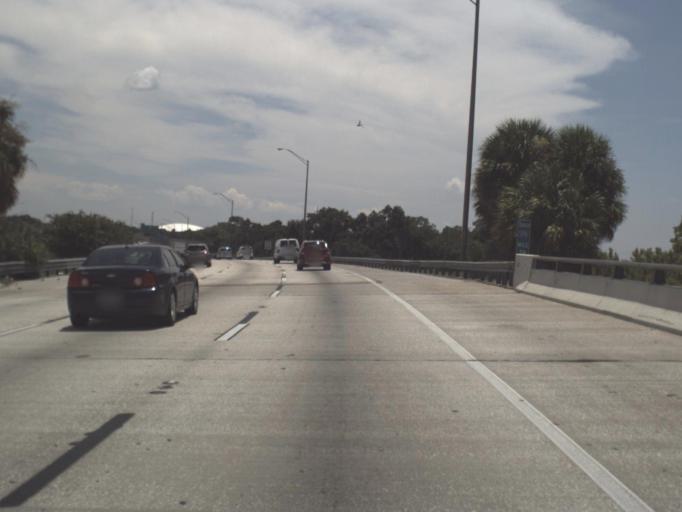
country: US
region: Florida
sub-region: Pinellas County
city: Lealman
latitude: 27.7993
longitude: -82.6629
